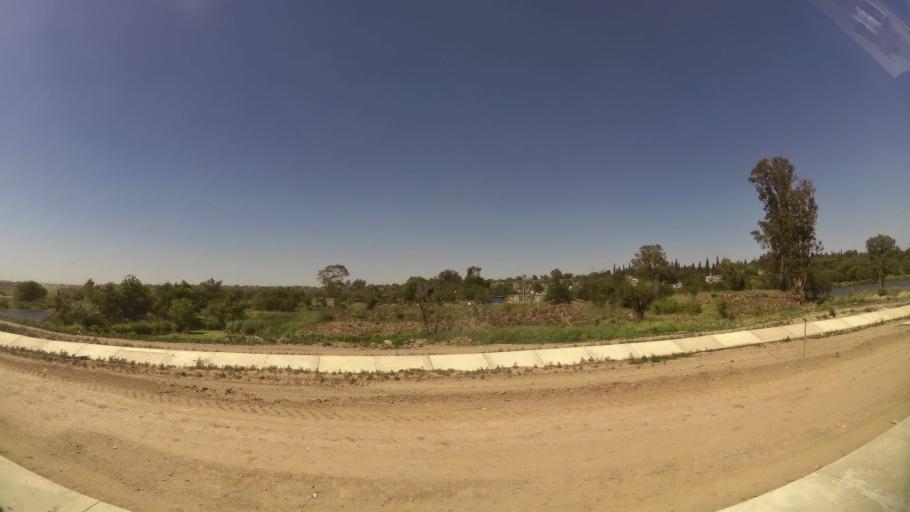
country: AR
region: Cordoba
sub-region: Departamento de Capital
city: Cordoba
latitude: -31.4081
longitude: -64.1241
